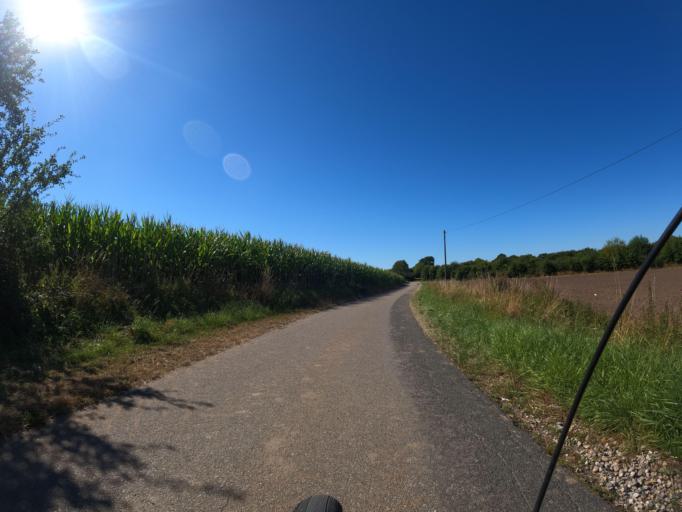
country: DE
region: Schleswig-Holstein
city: Steinbergkirche
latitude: 54.7776
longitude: 9.7627
